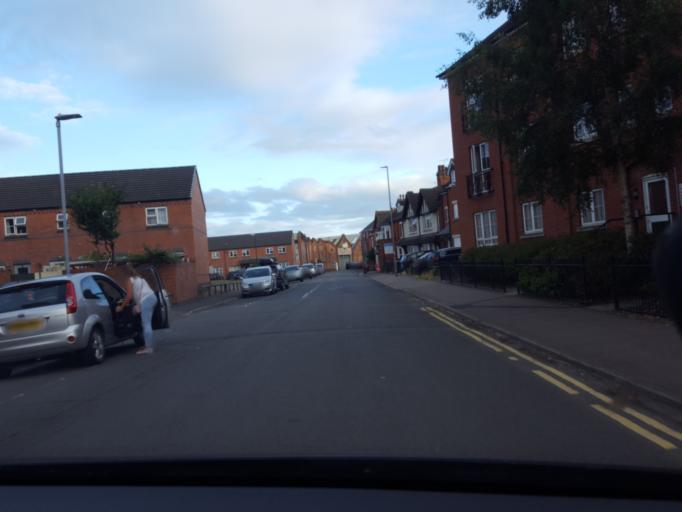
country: GB
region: England
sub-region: Leicestershire
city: Loughborough
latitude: 52.7716
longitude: -1.1930
